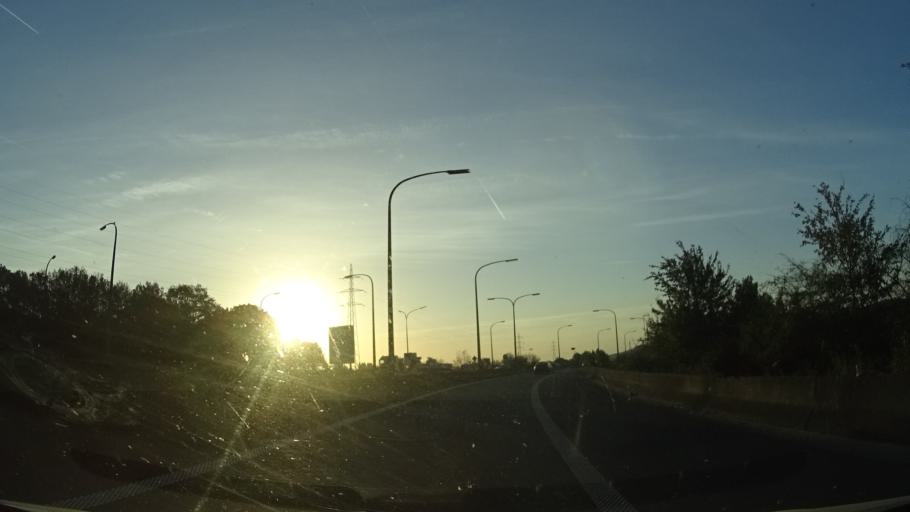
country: BE
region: Wallonia
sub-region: Province du Hainaut
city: Quaregnon
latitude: 50.4531
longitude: 3.9054
